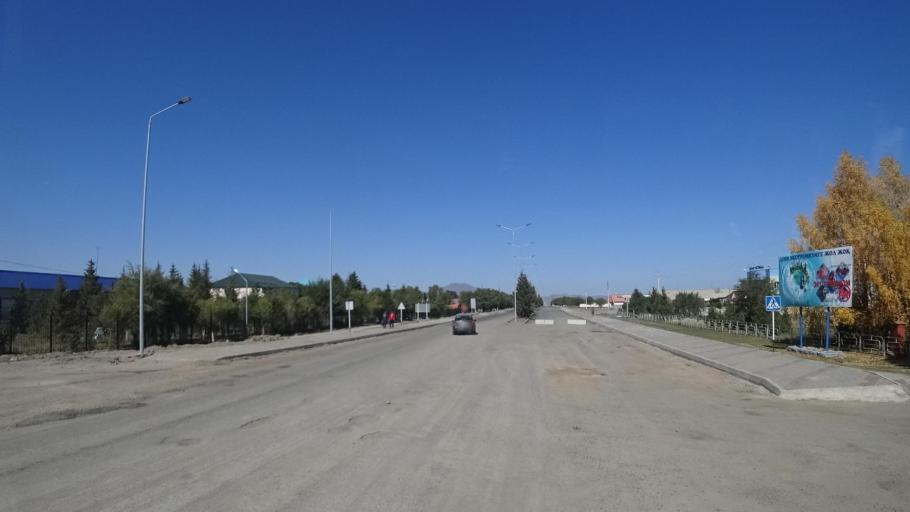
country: KZ
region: Almaty Oblysy
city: Kegen
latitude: 43.0156
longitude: 79.2307
